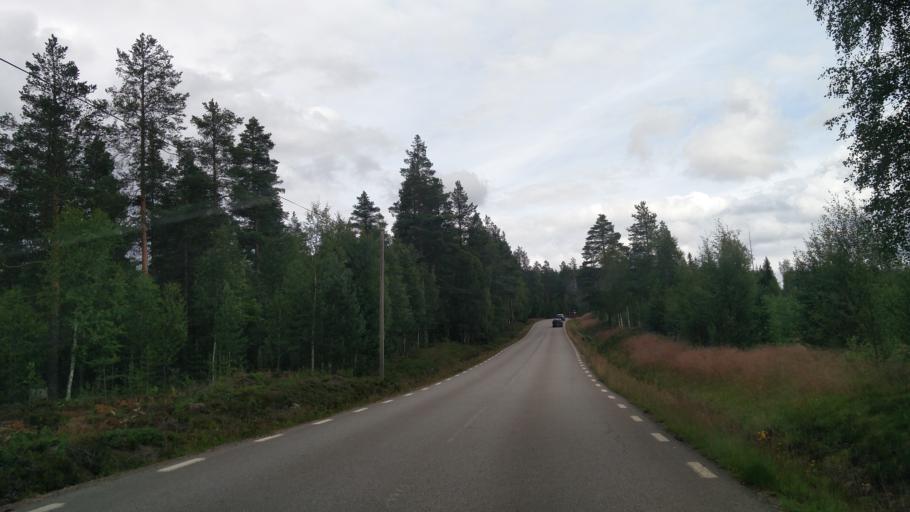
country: NO
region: Hedmark
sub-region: Trysil
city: Innbygda
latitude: 61.1758
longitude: 12.8498
